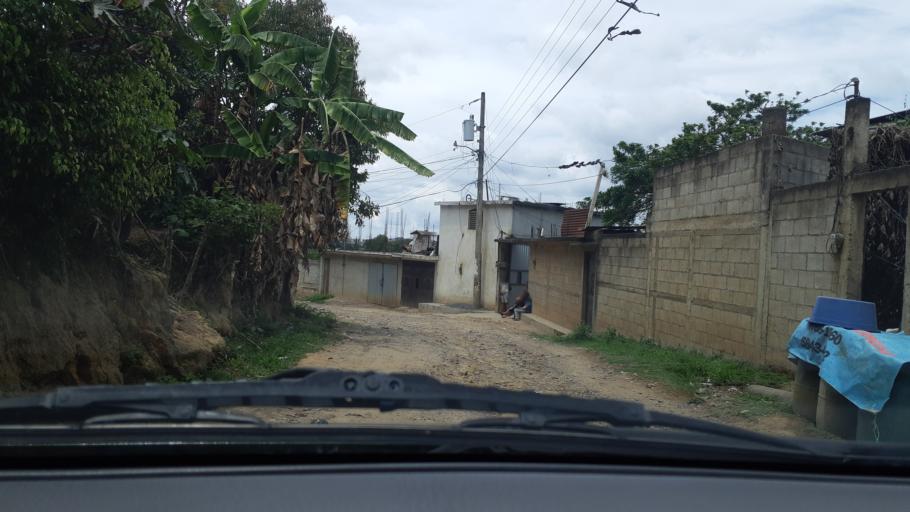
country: GT
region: Chimaltenango
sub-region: Municipio de Chimaltenango
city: Chimaltenango
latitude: 14.6637
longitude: -90.8494
